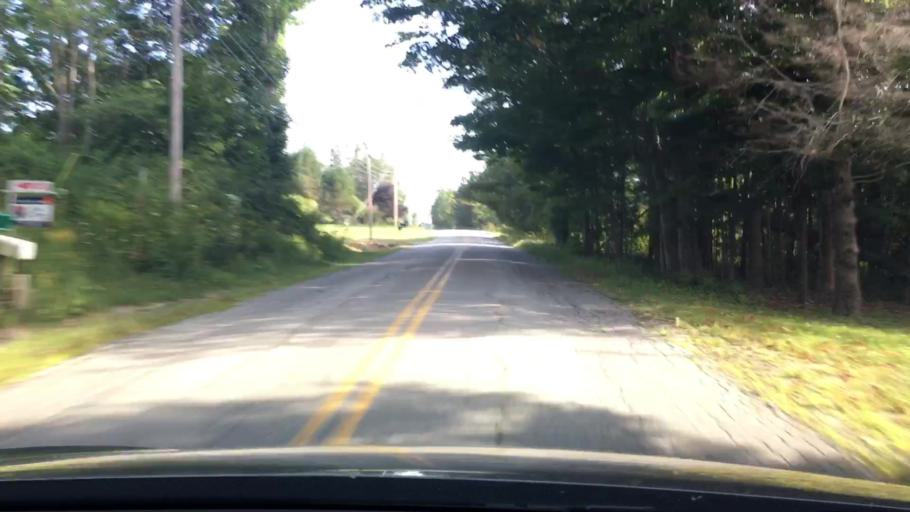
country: US
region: Maine
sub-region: Hancock County
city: Bucksport
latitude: 44.5473
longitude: -68.7973
